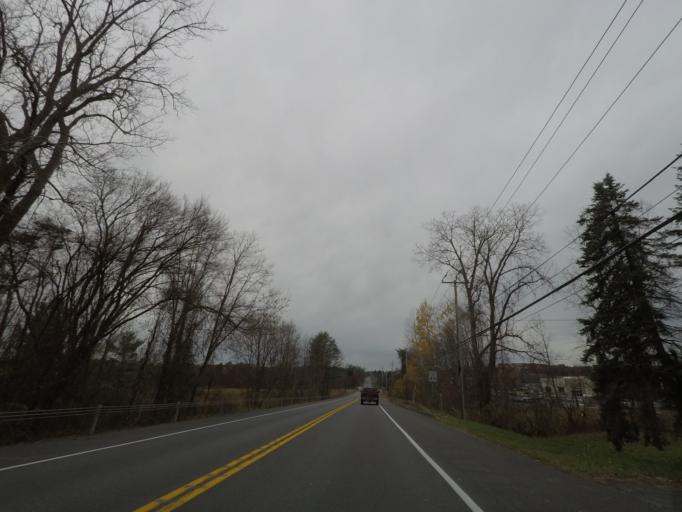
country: US
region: New York
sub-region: Saratoga County
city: Mechanicville
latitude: 42.8653
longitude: -73.7392
